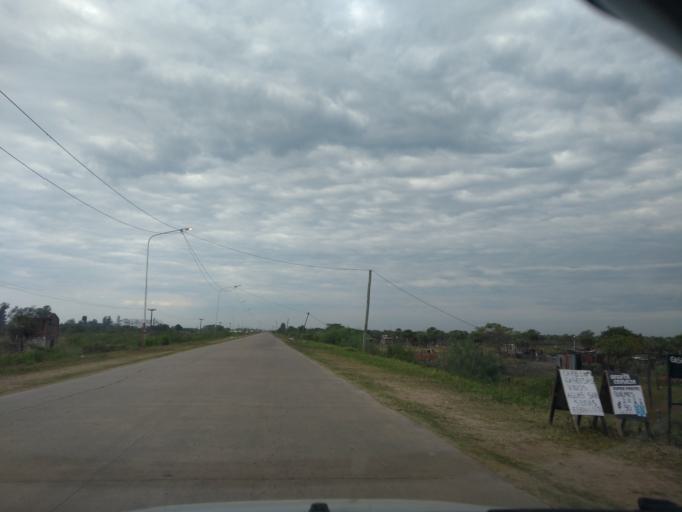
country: AR
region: Chaco
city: Puerto Vilelas
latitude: -27.5250
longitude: -58.9361
